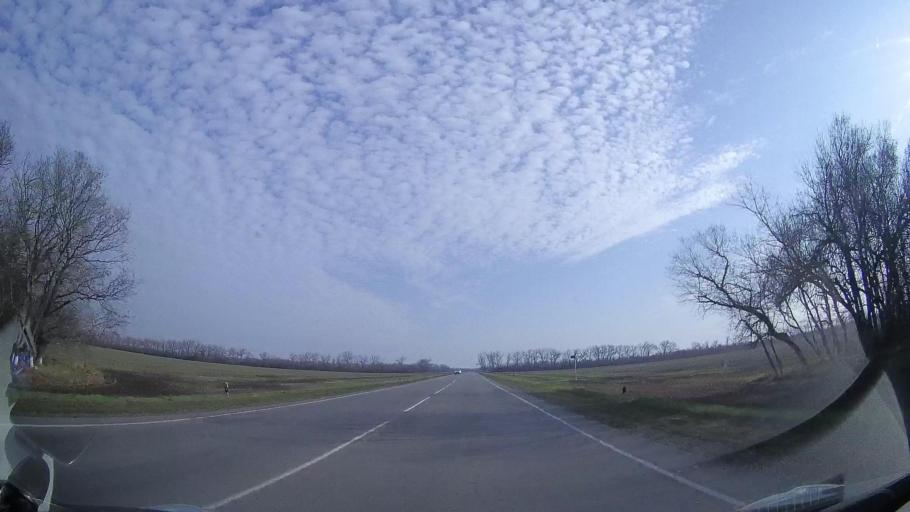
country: RU
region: Rostov
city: Tselina
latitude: 46.5229
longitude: 41.1291
